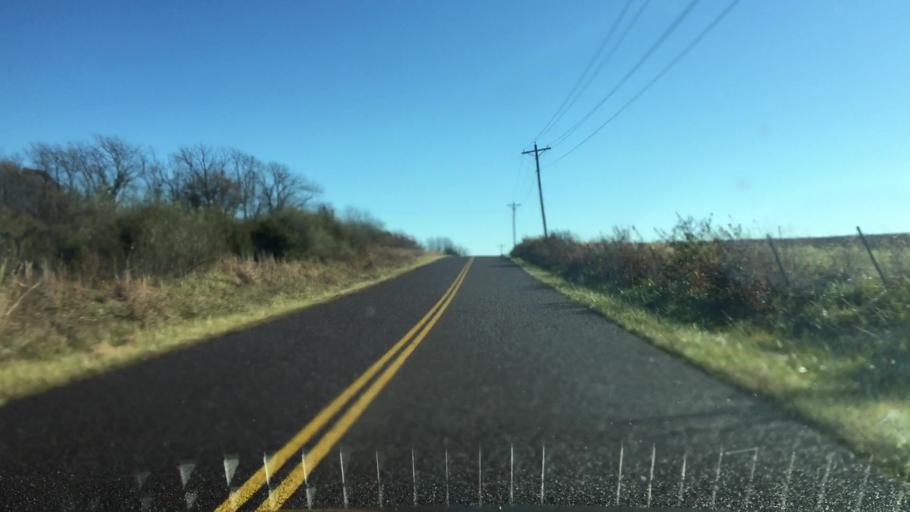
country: US
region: Missouri
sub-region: Boone County
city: Ashland
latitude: 38.8107
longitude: -92.2589
